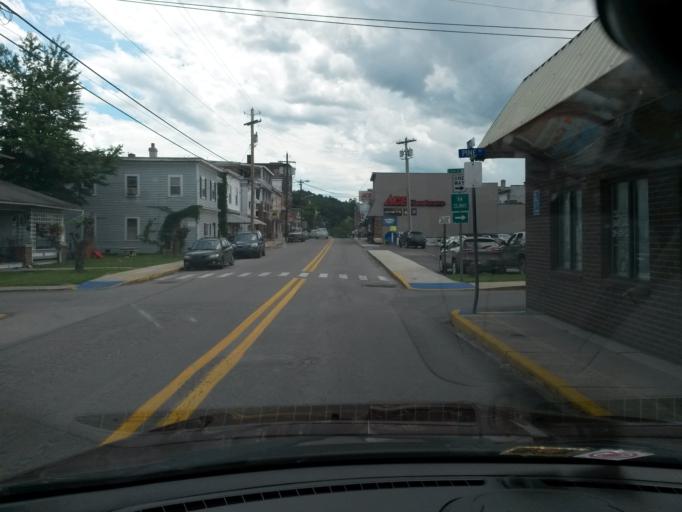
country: US
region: West Virginia
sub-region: Pendleton County
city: Franklin
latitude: 38.6435
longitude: -79.3307
